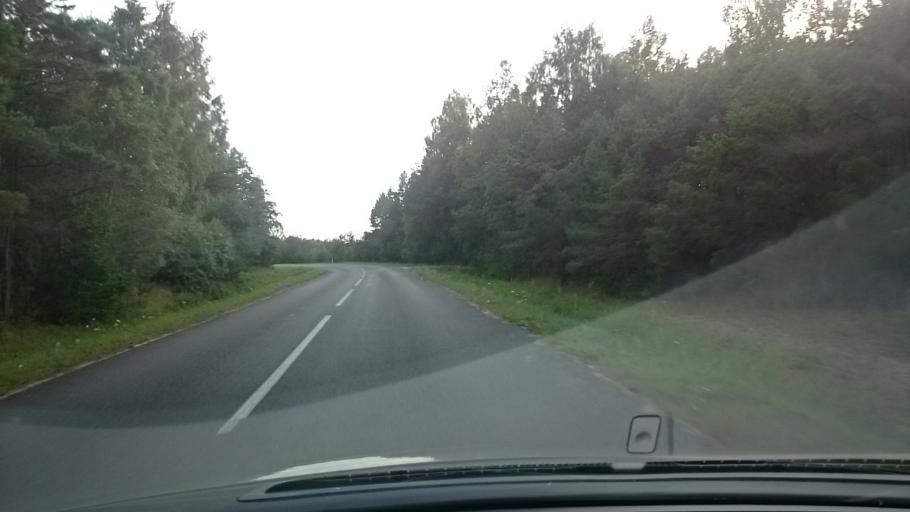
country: EE
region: Saare
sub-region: Kuressaare linn
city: Kuressaare
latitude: 58.4178
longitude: 22.1145
